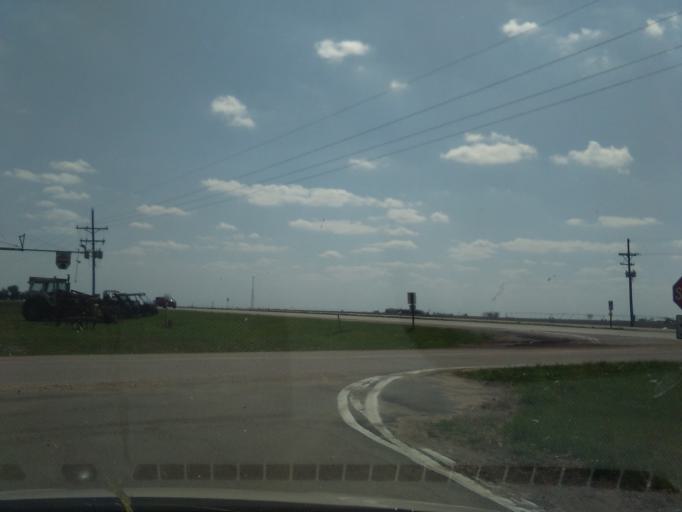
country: US
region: Nebraska
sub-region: Thayer County
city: Hebron
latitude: 40.2055
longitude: -97.5762
